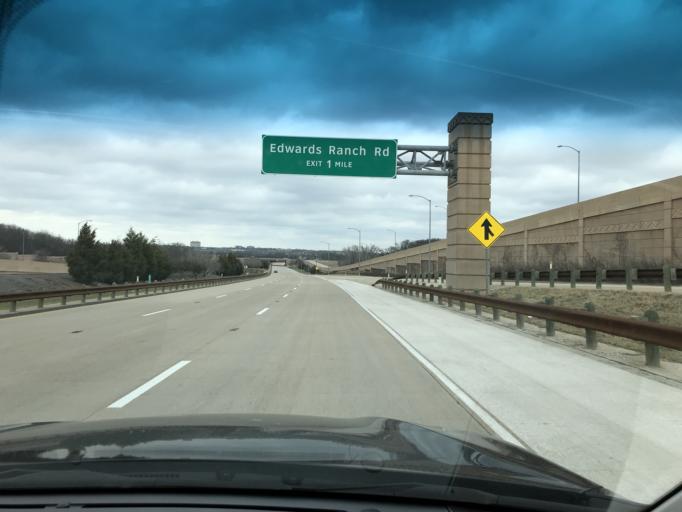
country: US
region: Texas
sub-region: Tarrant County
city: Benbrook
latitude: 32.6929
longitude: -97.4043
